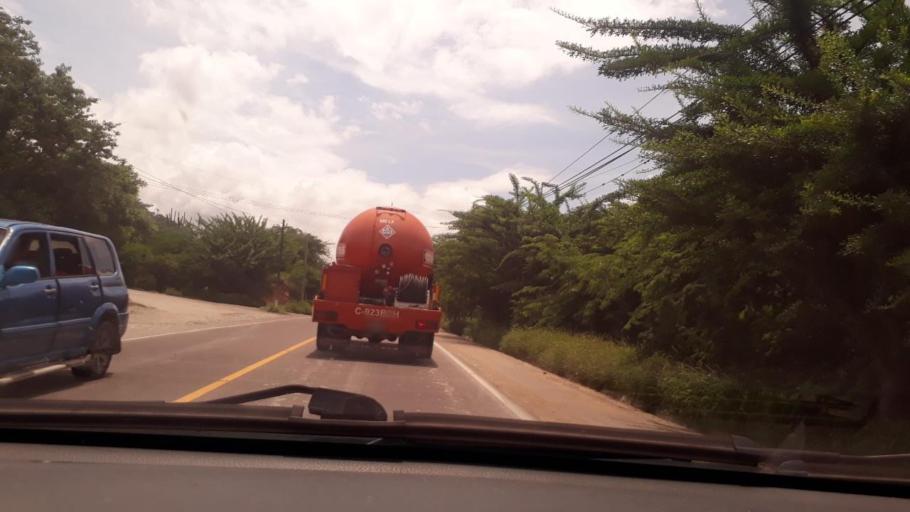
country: GT
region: Zacapa
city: Teculutan
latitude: 15.0176
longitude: -89.6511
